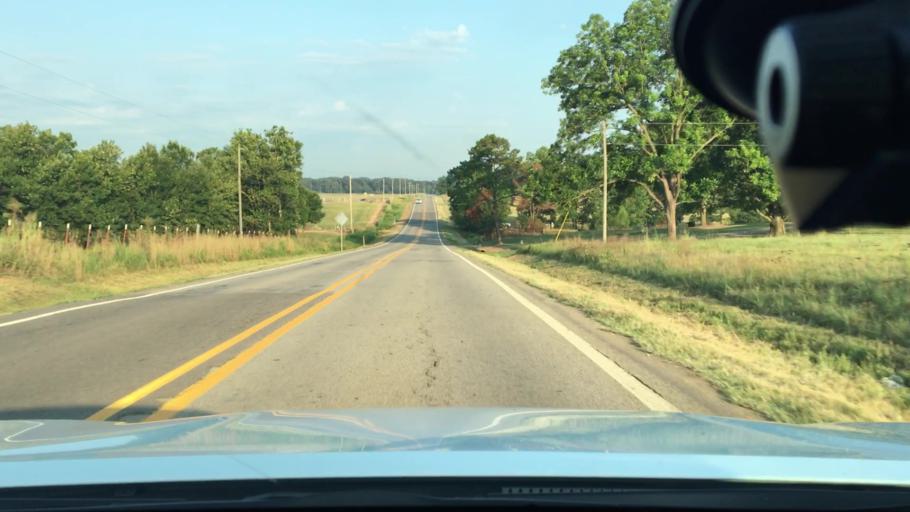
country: US
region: Arkansas
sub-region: Johnson County
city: Clarksville
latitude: 35.3790
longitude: -93.5458
